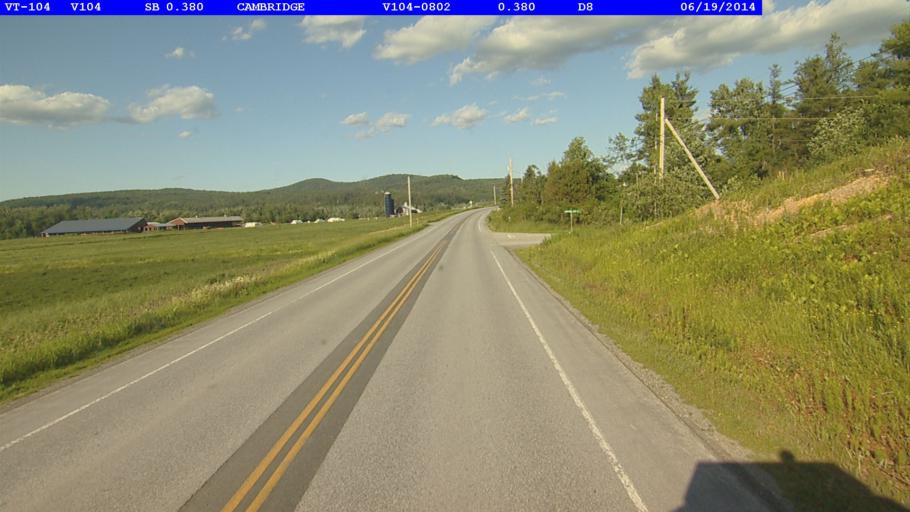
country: US
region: Vermont
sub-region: Chittenden County
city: Jericho
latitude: 44.6467
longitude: -72.8959
